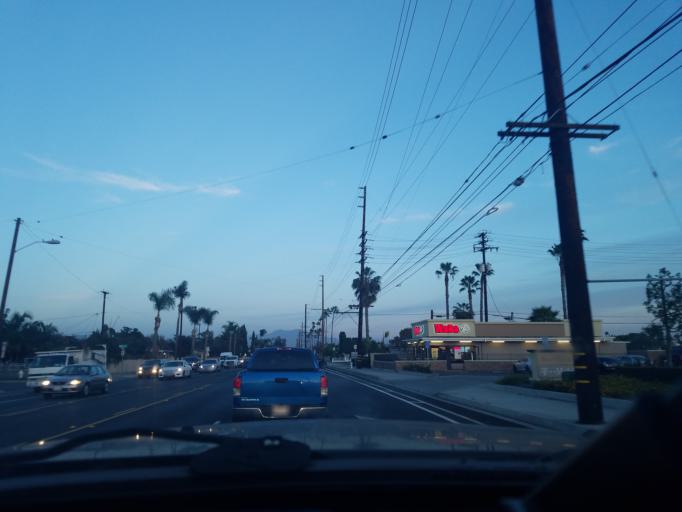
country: US
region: California
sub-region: Orange County
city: Santa Ana
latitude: 33.7161
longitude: -117.8840
